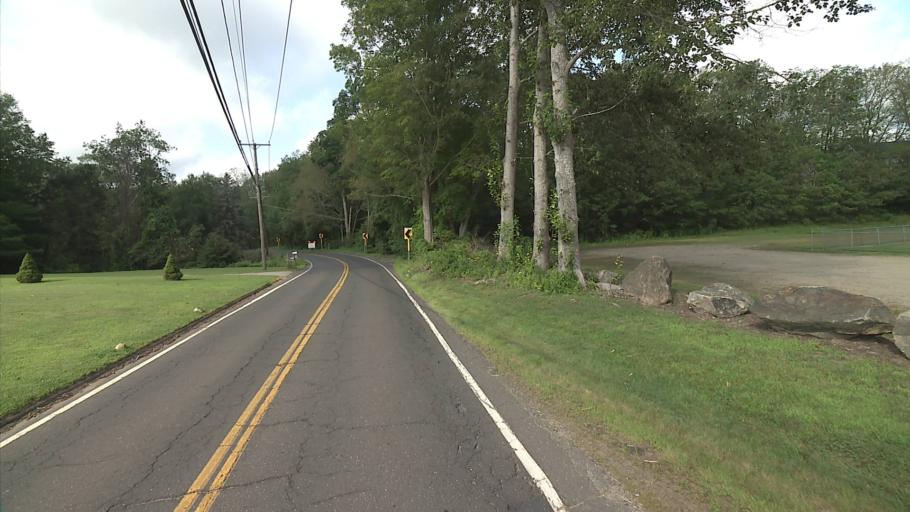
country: US
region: Connecticut
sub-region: Middlesex County
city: Moodus
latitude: 41.5159
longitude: -72.4264
